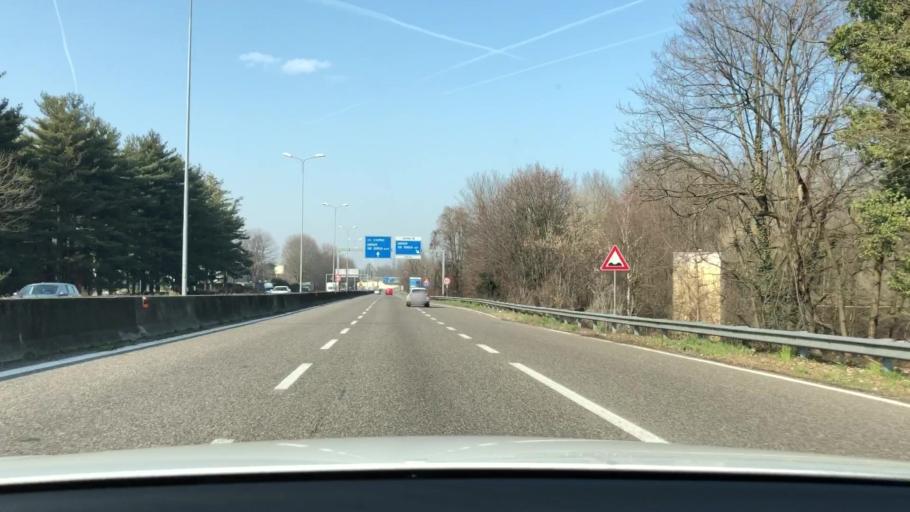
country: IT
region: Lombardy
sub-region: Provincia di Monza e Brianza
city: Barlassina
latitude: 45.6597
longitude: 9.1341
